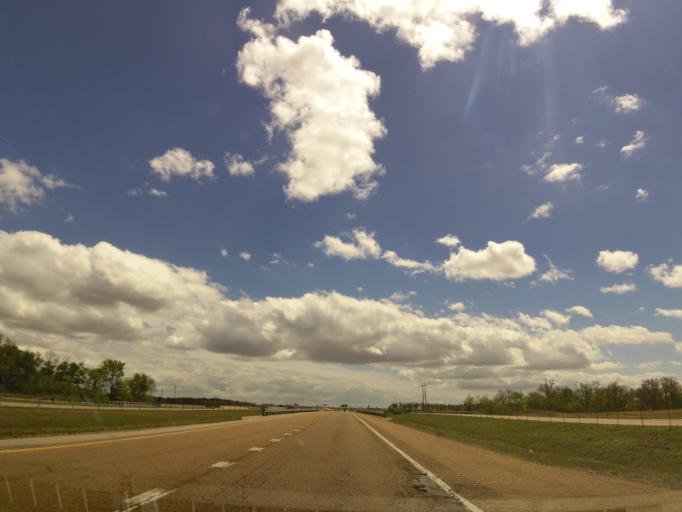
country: US
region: Arkansas
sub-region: Poinsett County
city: Marked Tree
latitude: 35.4036
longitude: -90.2793
